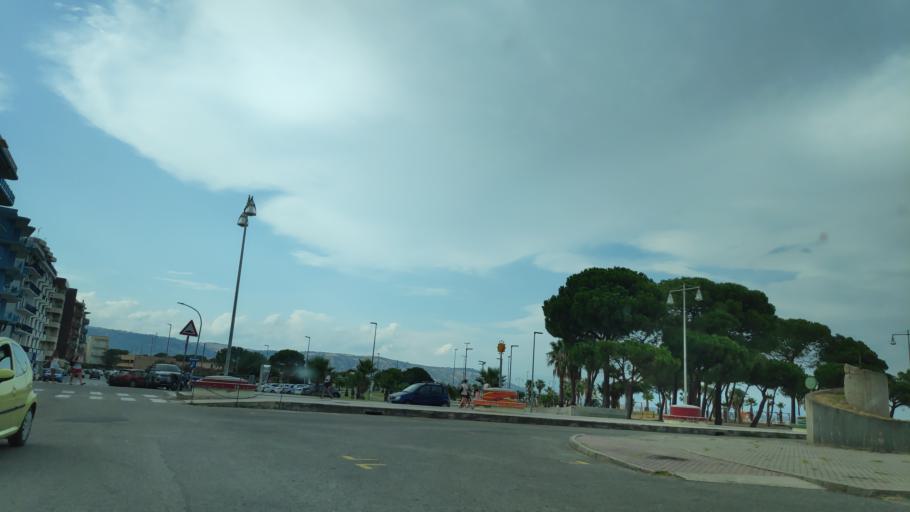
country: IT
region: Calabria
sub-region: Provincia di Catanzaro
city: Soverato Marina
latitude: 38.6856
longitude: 16.5552
